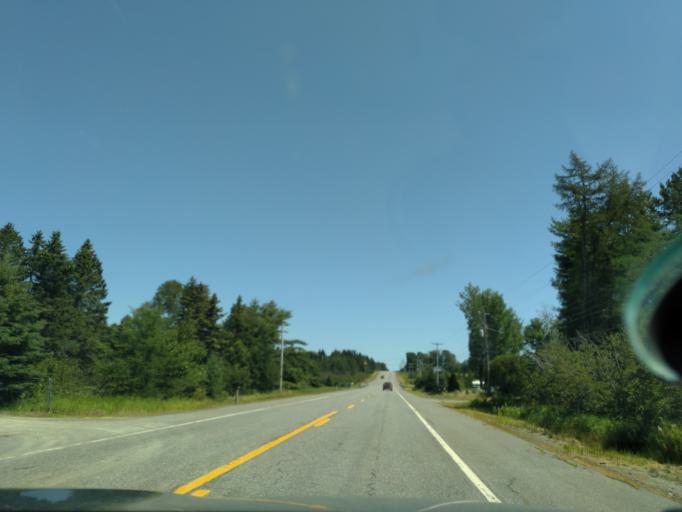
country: US
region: Maine
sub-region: Washington County
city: East Machias
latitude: 44.7595
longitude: -67.2219
